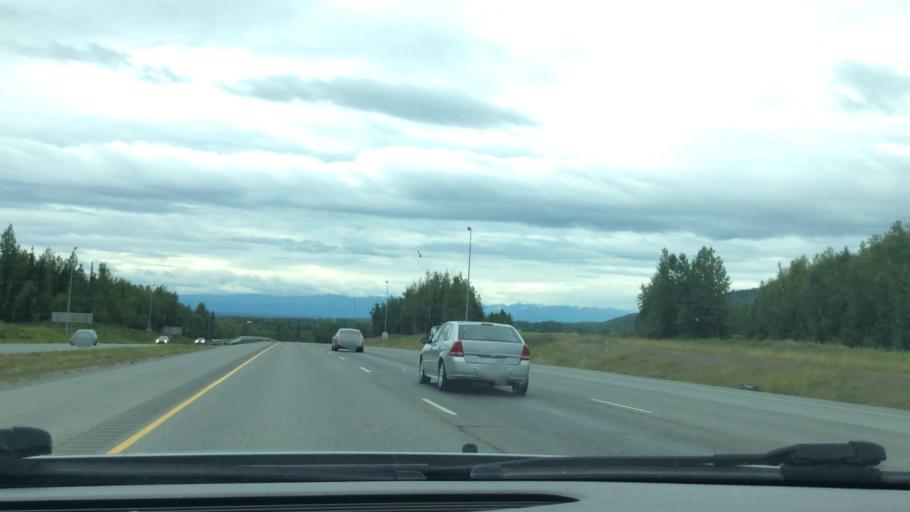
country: US
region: Alaska
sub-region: Anchorage Municipality
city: Eagle River
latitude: 61.3000
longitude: -149.5883
